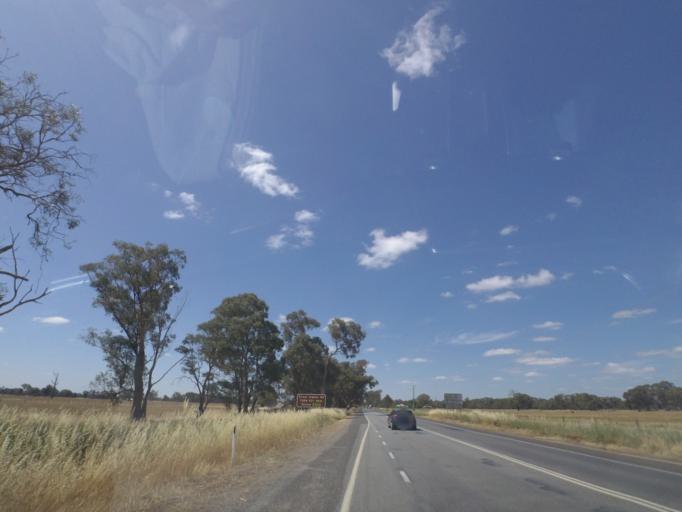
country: AU
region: Victoria
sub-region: Wangaratta
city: Wangaratta
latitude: -36.4053
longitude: 146.2733
